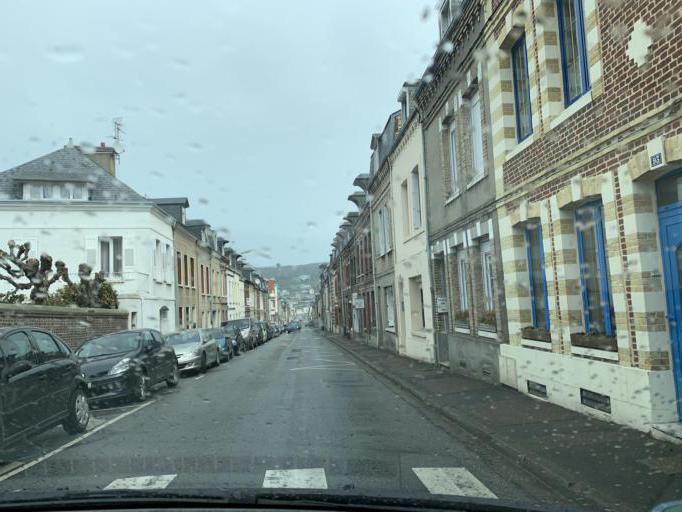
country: FR
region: Haute-Normandie
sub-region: Departement de la Seine-Maritime
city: Fecamp
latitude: 49.7578
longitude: 0.3637
